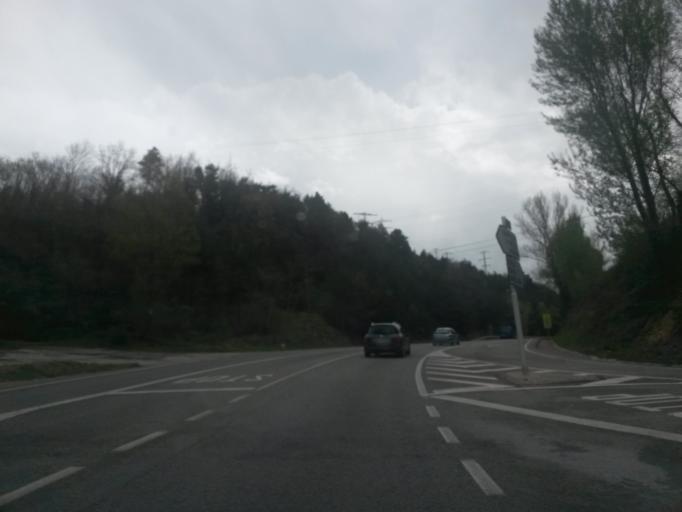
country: ES
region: Catalonia
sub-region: Provincia de Barcelona
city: Vallcebre
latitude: 42.1747
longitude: 1.8616
